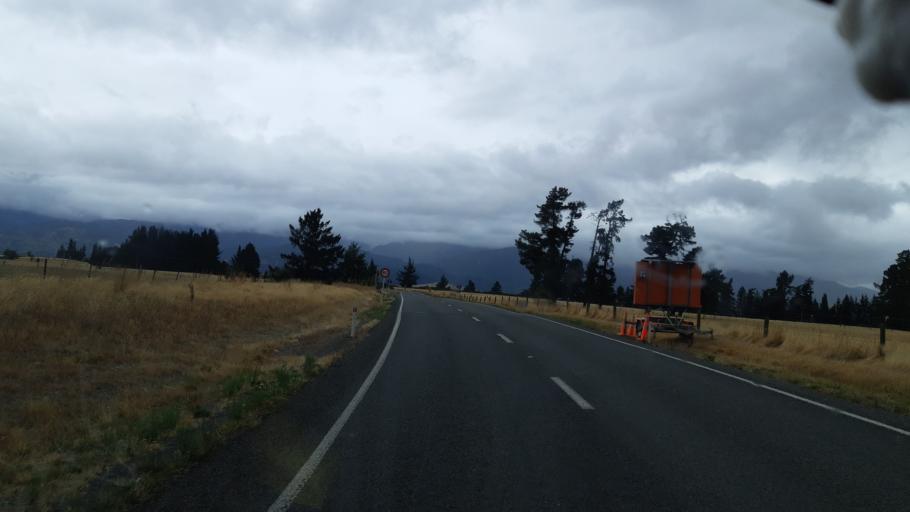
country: NZ
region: Canterbury
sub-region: Hurunui District
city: Amberley
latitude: -42.5863
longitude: 172.7777
